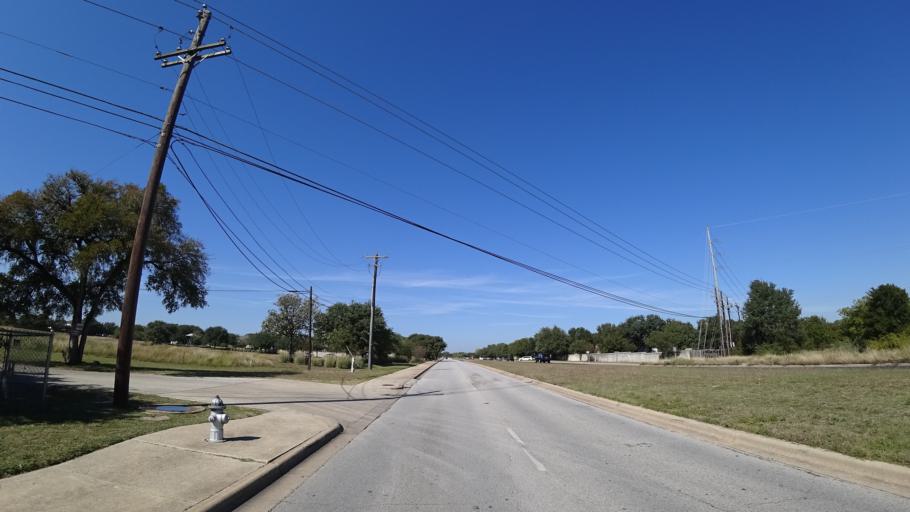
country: US
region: Texas
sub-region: Travis County
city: Shady Hollow
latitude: 30.1922
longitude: -97.8582
